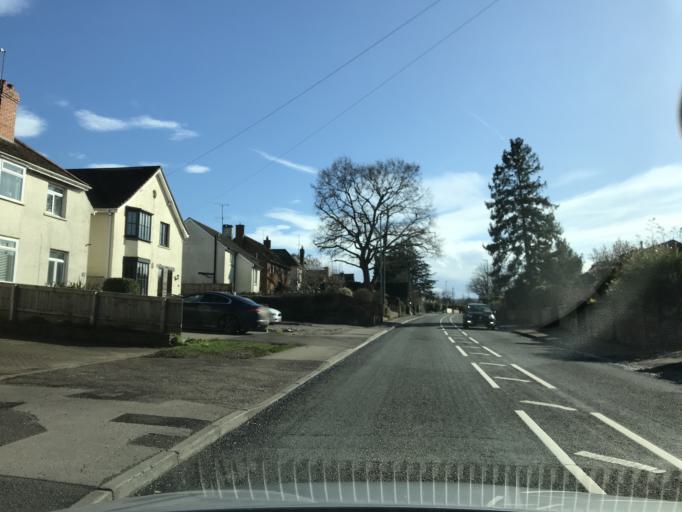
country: GB
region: England
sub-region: Somerset
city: Taunton
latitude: 51.0034
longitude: -3.0873
